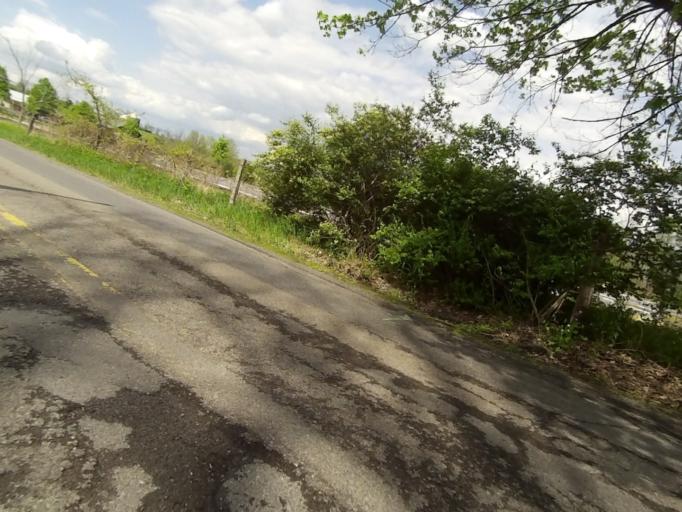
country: US
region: Pennsylvania
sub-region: Centre County
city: Houserville
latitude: 40.8115
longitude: -77.8386
